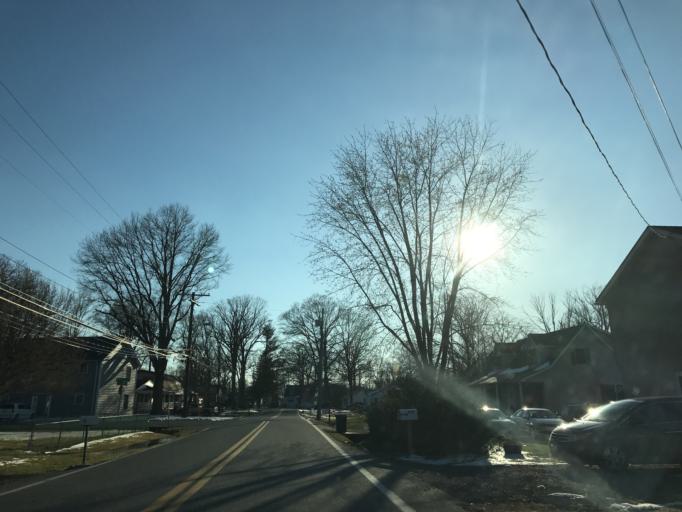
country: US
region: Maryland
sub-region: Baltimore County
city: Essex
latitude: 39.2888
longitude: -76.4430
